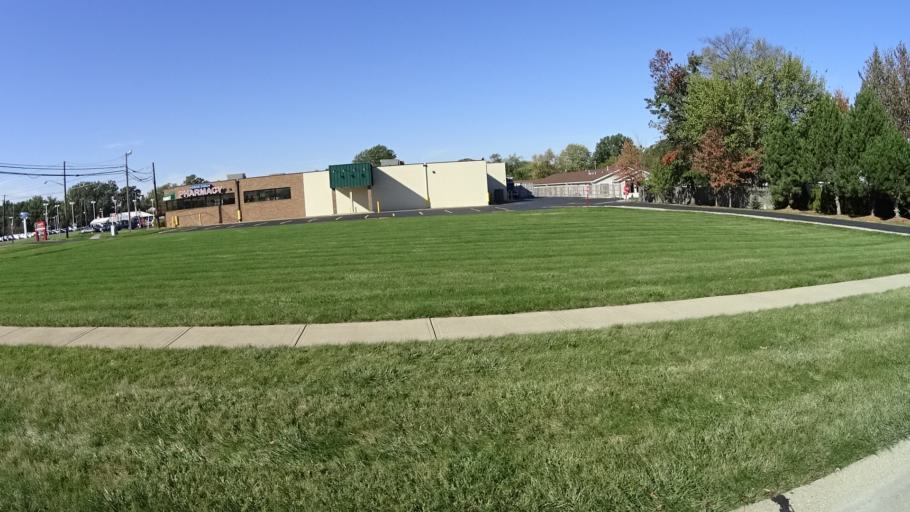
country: US
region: Ohio
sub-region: Lorain County
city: Vermilion-on-the-Lake
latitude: 41.4257
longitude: -82.3355
